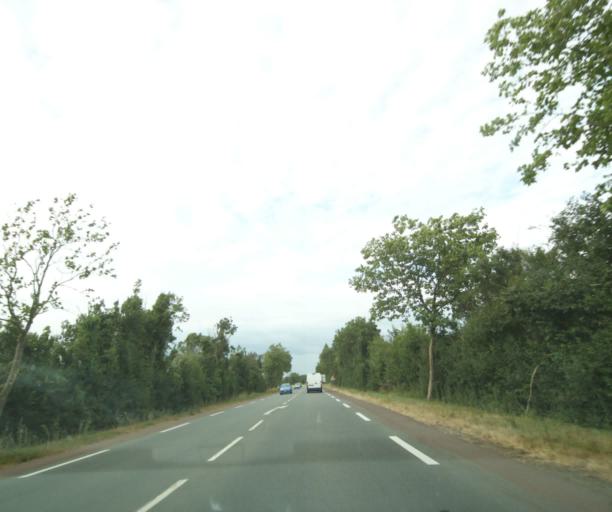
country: FR
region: Poitou-Charentes
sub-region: Departement de la Charente-Maritime
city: Marans
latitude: 46.2821
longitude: -0.9954
